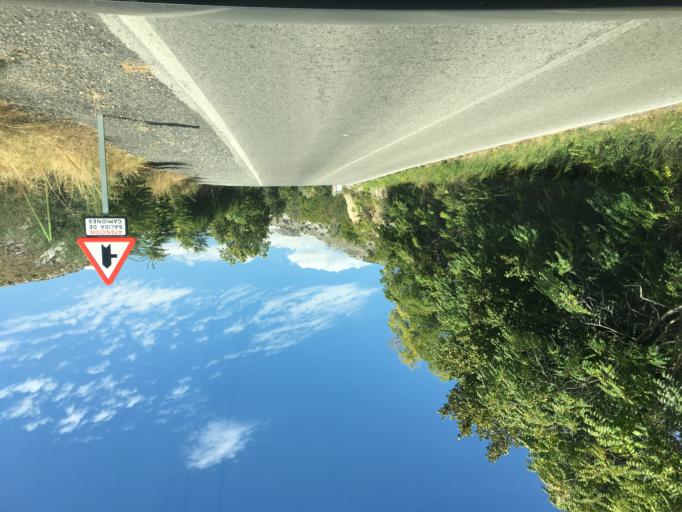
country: ES
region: Andalusia
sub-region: Provincia de Granada
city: Huetor Santillan
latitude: 37.2271
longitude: -3.5048
